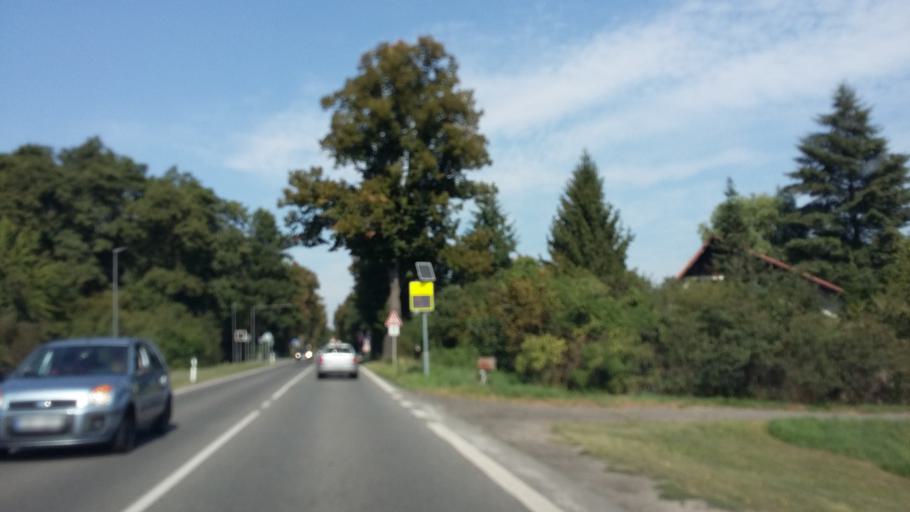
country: CZ
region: Central Bohemia
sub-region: Okres Nymburk
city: Podebrady
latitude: 50.1352
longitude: 15.1070
